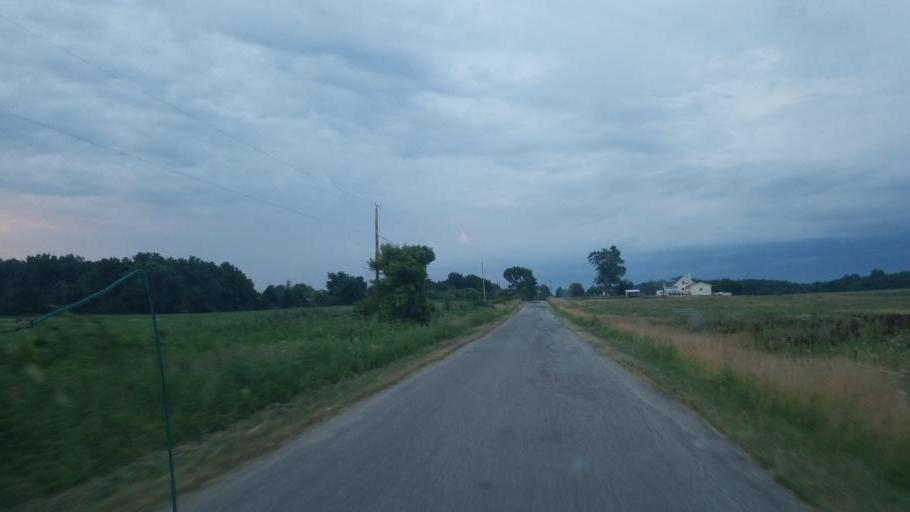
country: US
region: Ohio
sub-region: Defiance County
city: Hicksville
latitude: 41.3320
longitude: -84.8302
